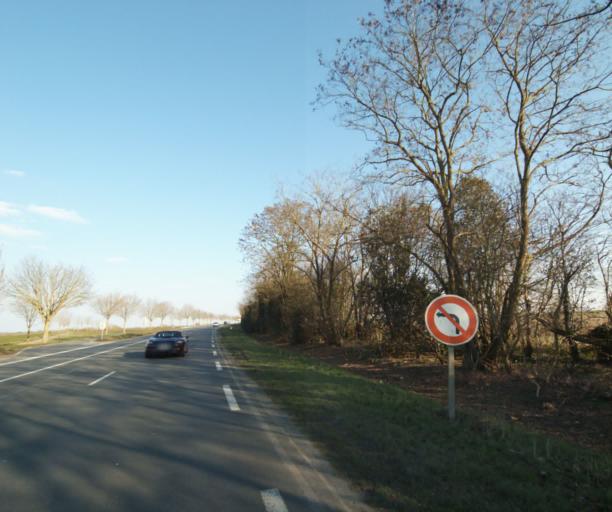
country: FR
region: Poitou-Charentes
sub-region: Departement des Deux-Sevres
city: Vouille
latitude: 46.3182
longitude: -0.3963
